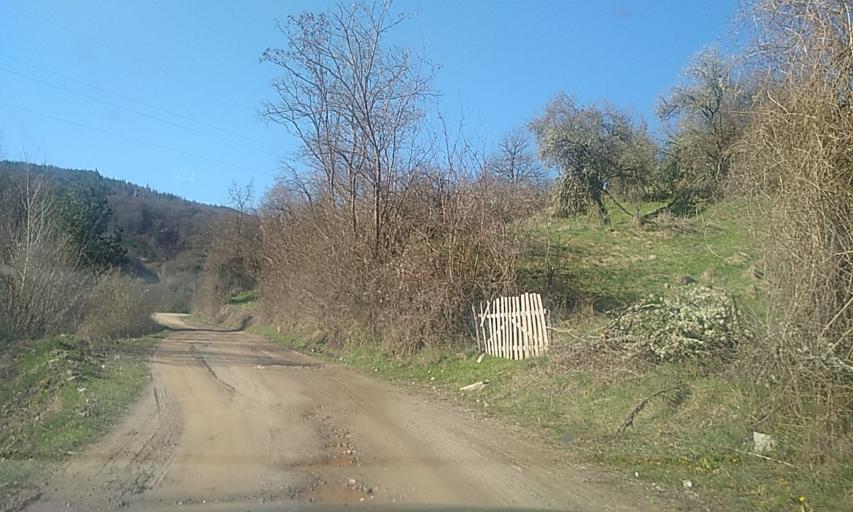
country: RS
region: Central Serbia
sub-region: Pcinjski Okrug
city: Bosilegrad
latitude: 42.3551
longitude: 22.4051
